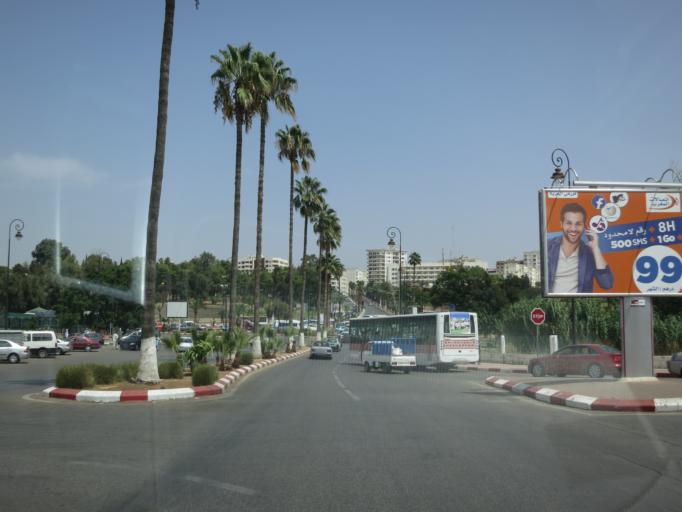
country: MA
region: Meknes-Tafilalet
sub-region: Meknes
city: Meknes
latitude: 33.8947
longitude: -5.5572
